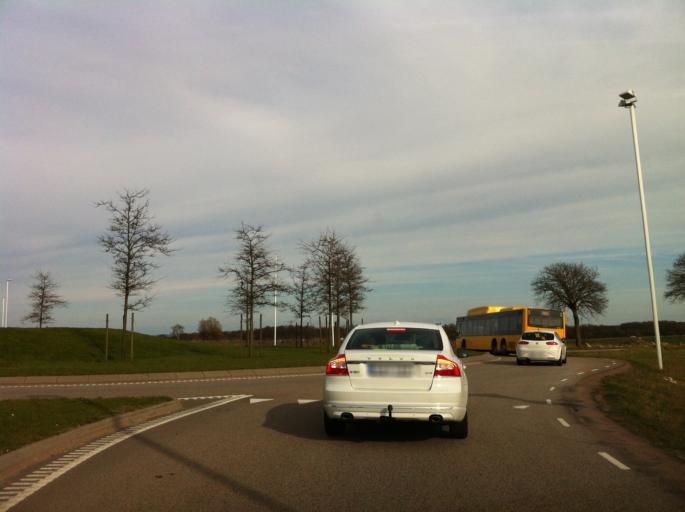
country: SE
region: Skane
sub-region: Helsingborg
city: Odakra
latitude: 56.0913
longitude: 12.7676
